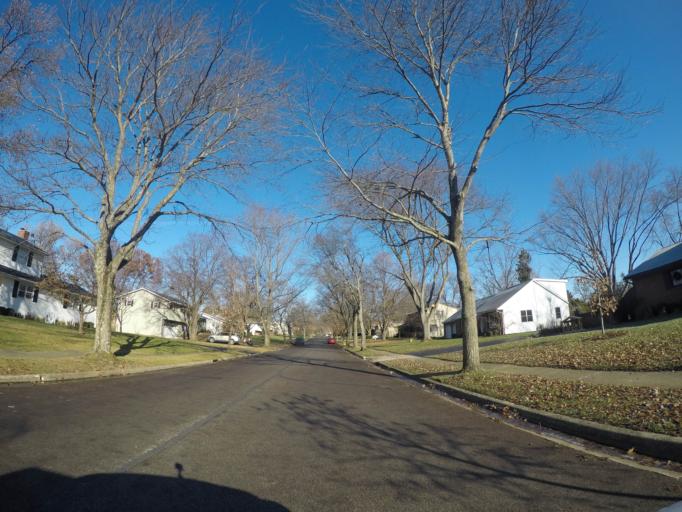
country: US
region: Ohio
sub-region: Franklin County
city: Upper Arlington
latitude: 40.0361
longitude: -83.0654
